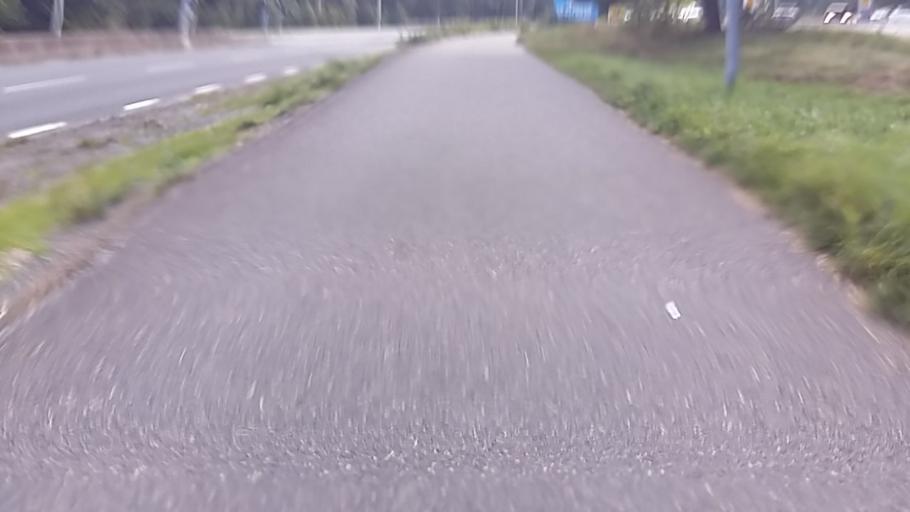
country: SE
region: Joenkoeping
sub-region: Jonkopings Kommun
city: Odensjo
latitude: 57.7465
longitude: 14.1564
